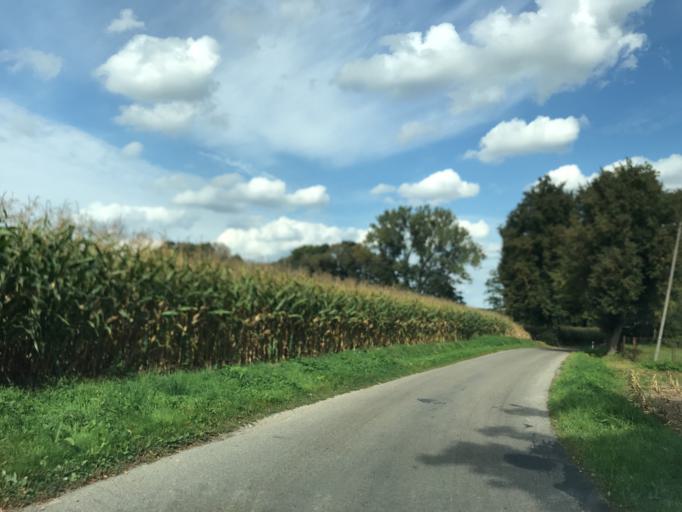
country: PL
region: Warmian-Masurian Voivodeship
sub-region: Powiat ilawski
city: Lubawa
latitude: 53.4108
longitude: 19.7530
